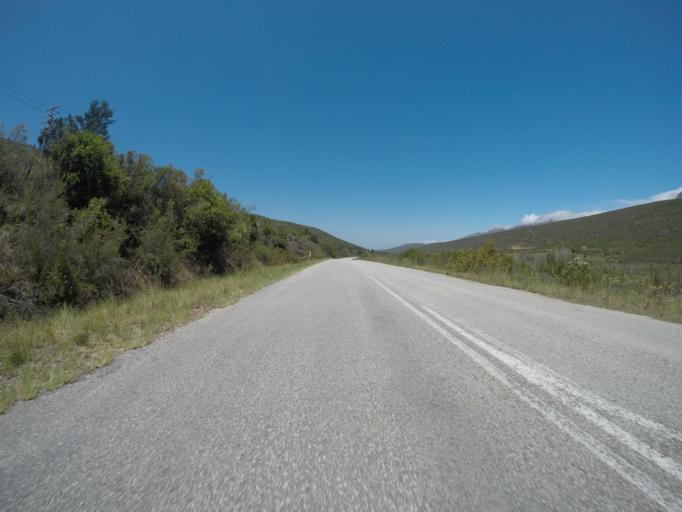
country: ZA
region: Eastern Cape
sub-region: Cacadu District Municipality
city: Kareedouw
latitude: -33.8726
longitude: 24.0427
